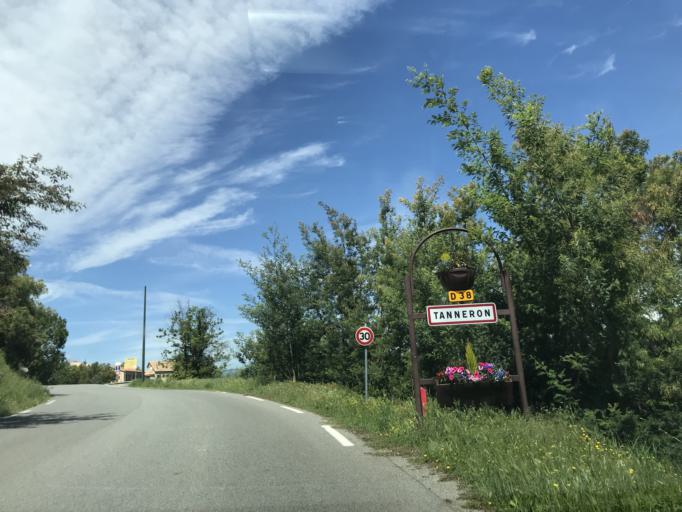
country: FR
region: Provence-Alpes-Cote d'Azur
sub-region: Departement du Var
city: Tanneron
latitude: 43.5892
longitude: 6.8779
